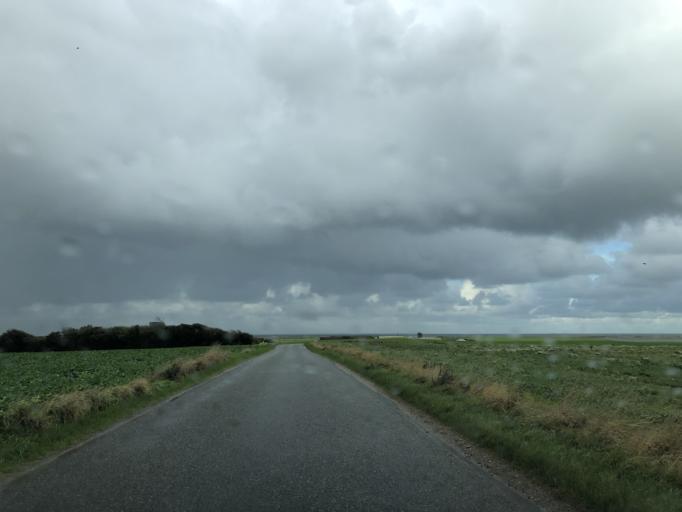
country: DK
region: Central Jutland
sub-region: Lemvig Kommune
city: Harboore
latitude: 56.5464
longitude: 8.1598
